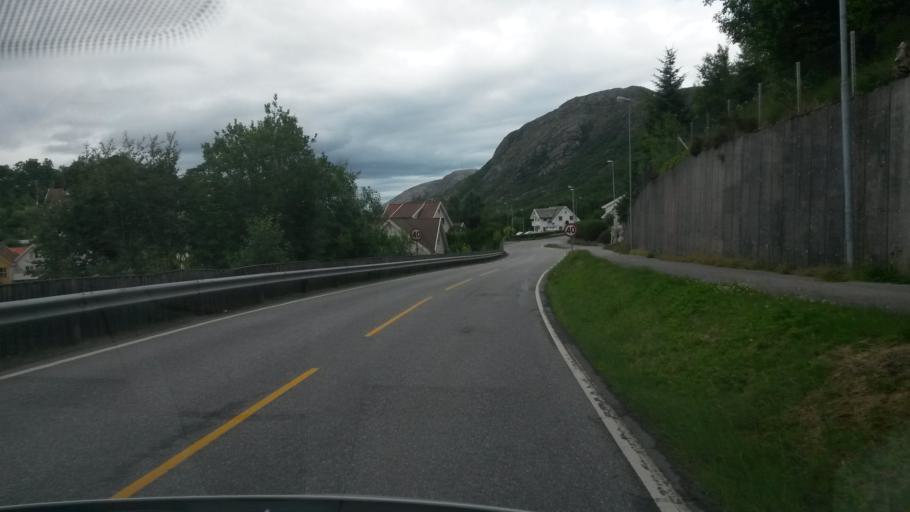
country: NO
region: Rogaland
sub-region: Sandnes
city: Sandnes
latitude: 58.8785
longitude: 5.7733
